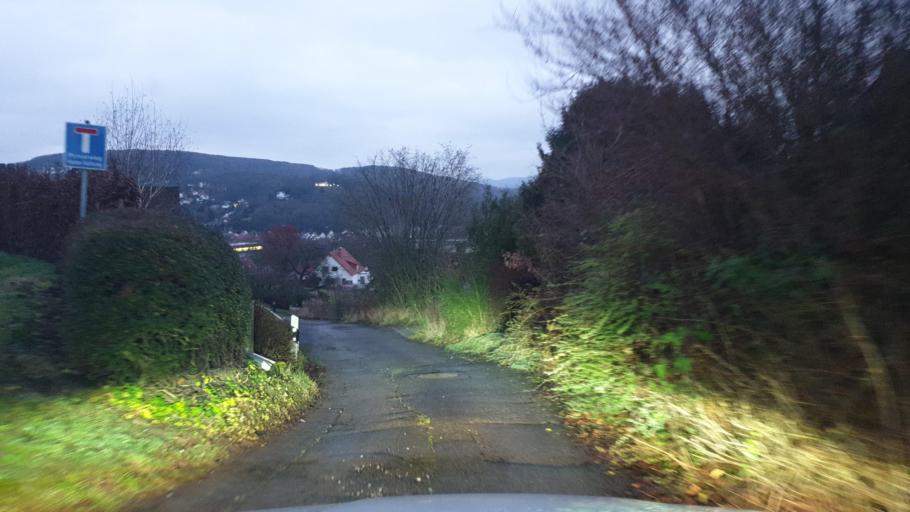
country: DE
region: North Rhine-Westphalia
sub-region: Regierungsbezirk Detmold
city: Vlotho
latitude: 52.1617
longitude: 8.8754
